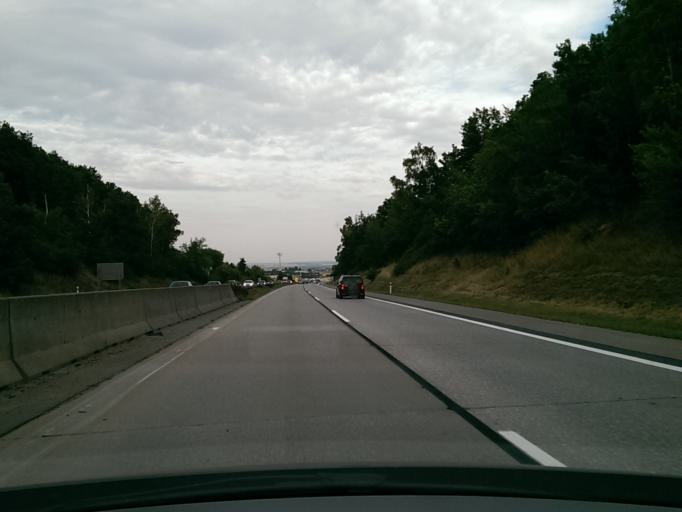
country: CZ
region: South Moravian
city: Troubsko
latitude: 49.1841
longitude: 16.4715
